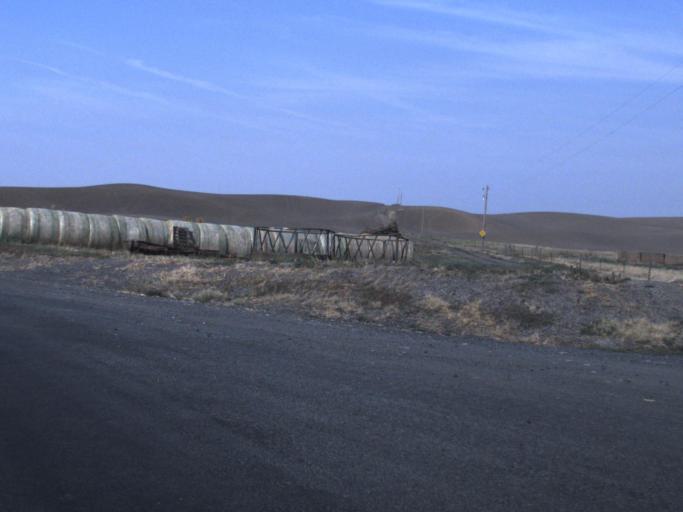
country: US
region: Idaho
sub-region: Benewah County
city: Plummer
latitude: 47.1961
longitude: -117.1410
